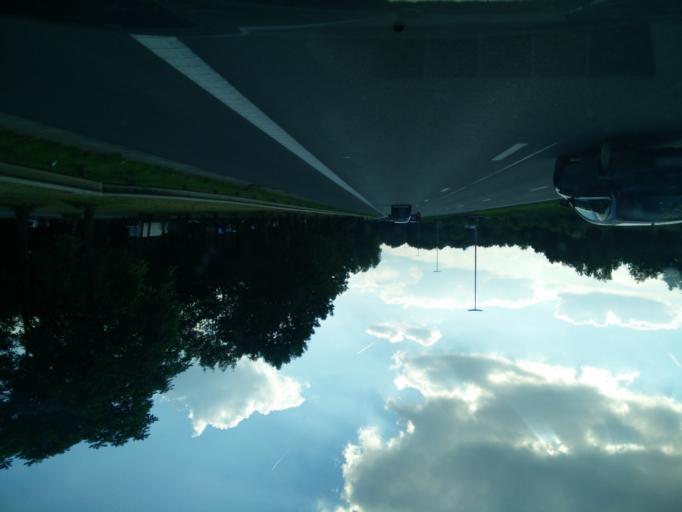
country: BE
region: Wallonia
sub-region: Province du Brabant Wallon
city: Braine-le-Chateau
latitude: 50.6971
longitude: 4.2868
